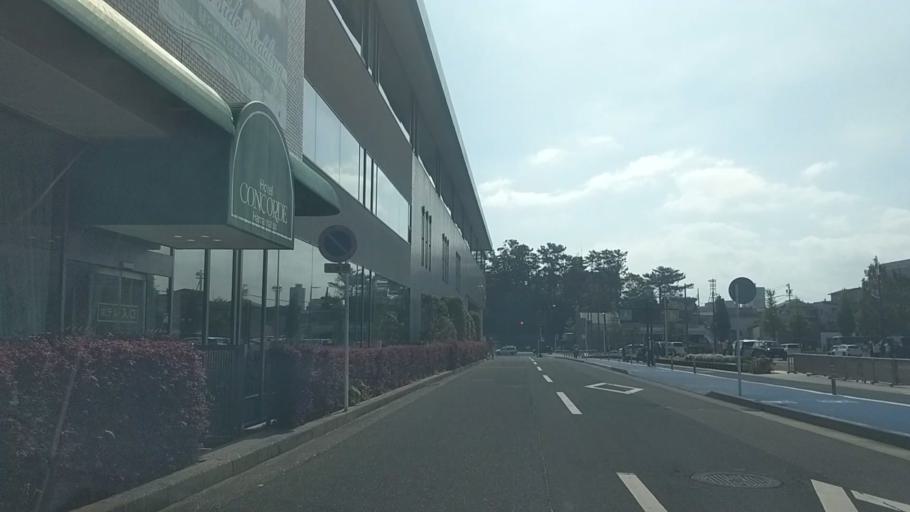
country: JP
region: Shizuoka
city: Hamamatsu
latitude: 34.7139
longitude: 137.7262
